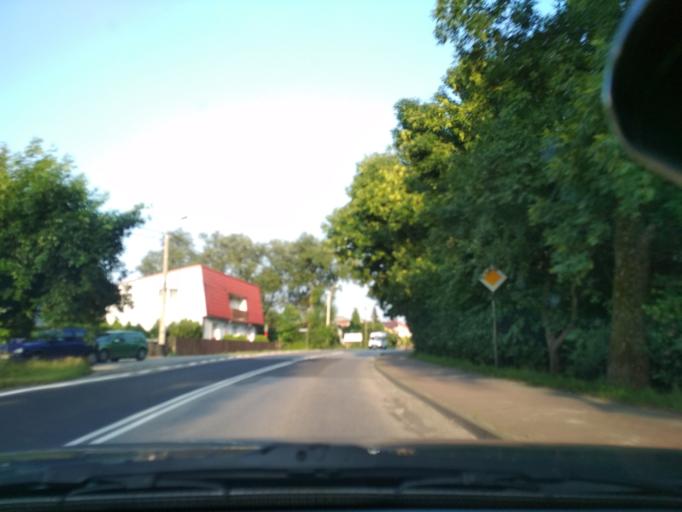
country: PL
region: Silesian Voivodeship
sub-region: Powiat zawiercianski
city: Ogrodzieniec
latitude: 50.4539
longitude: 19.5102
